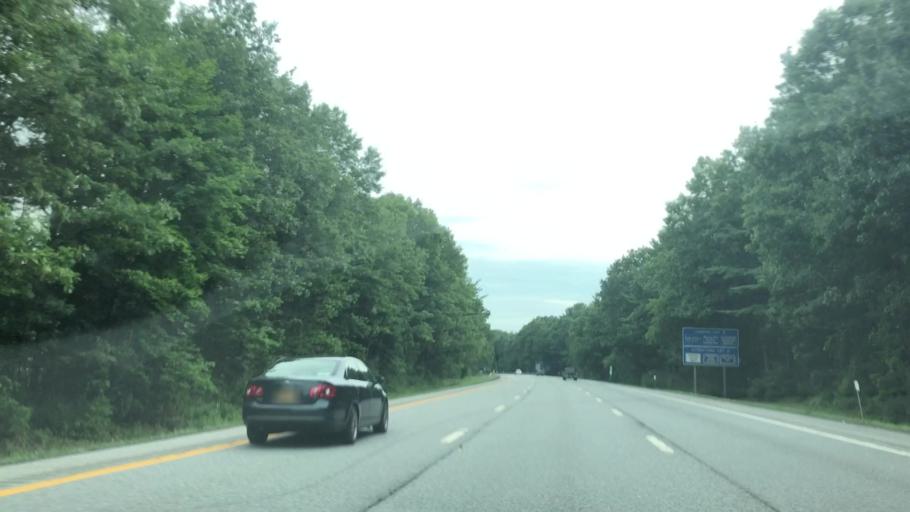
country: US
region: New York
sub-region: Saratoga County
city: Saratoga Springs
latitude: 43.1099
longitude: -73.7509
